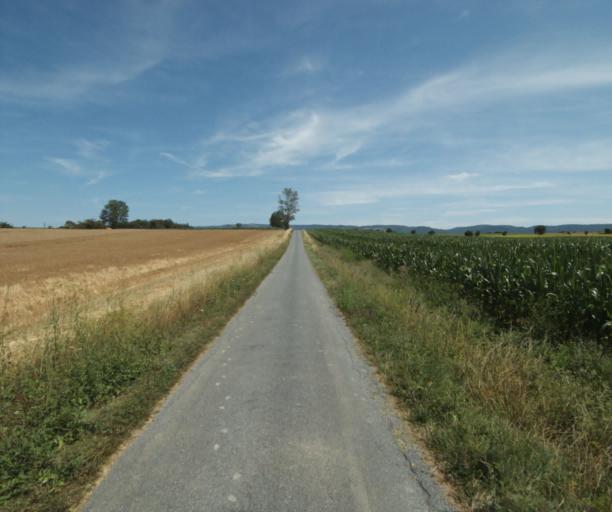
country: FR
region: Midi-Pyrenees
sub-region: Departement de la Haute-Garonne
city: Revel
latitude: 43.5106
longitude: 2.0137
